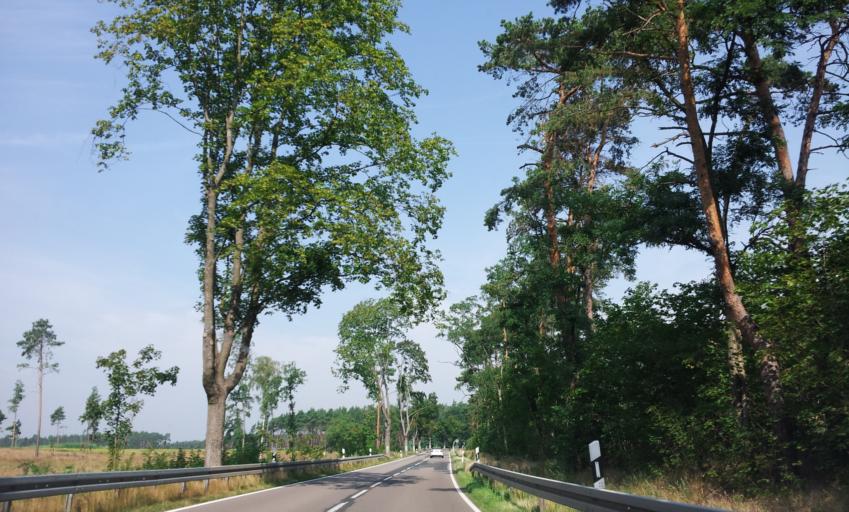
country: DE
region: Brandenburg
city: Linthe
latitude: 52.1211
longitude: 12.8112
